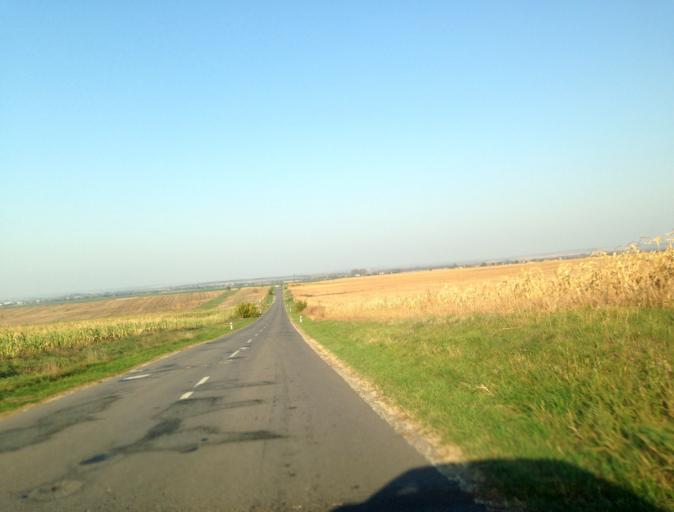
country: SK
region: Nitriansky
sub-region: Okres Komarno
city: Hurbanovo
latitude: 47.9026
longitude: 18.2788
